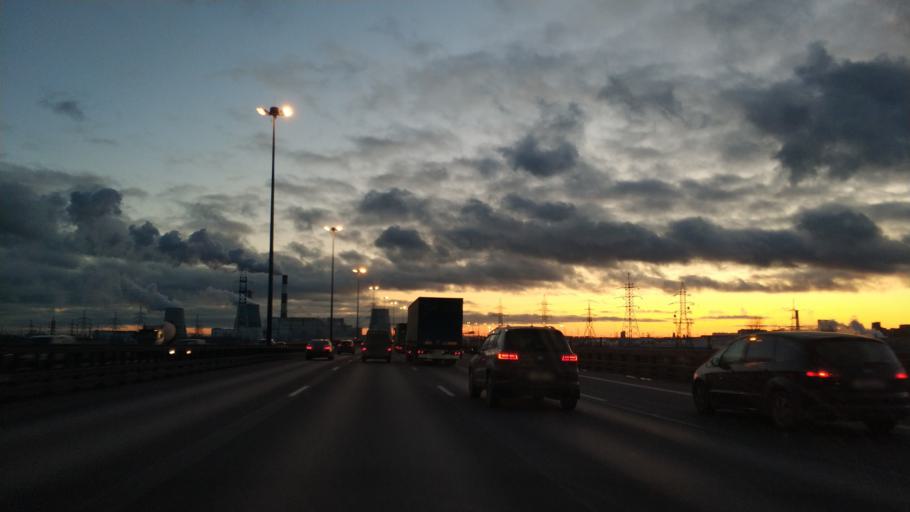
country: RU
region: St.-Petersburg
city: Obukhovo
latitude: 59.8440
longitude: 30.4568
